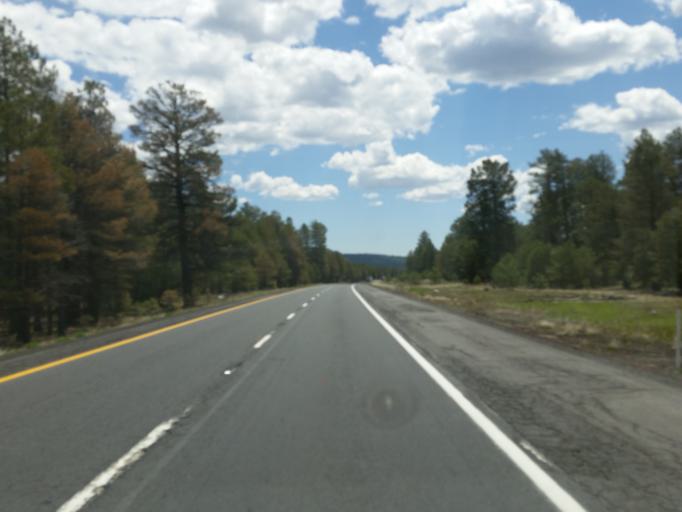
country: US
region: Arizona
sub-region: Coconino County
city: Parks
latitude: 35.2480
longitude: -111.8560
